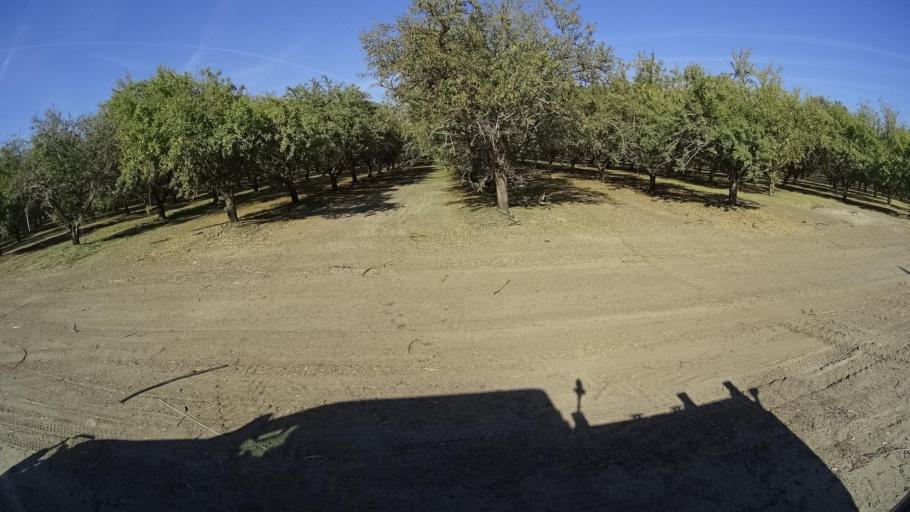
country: US
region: California
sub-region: Kern County
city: Wasco
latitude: 35.6669
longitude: -119.3608
